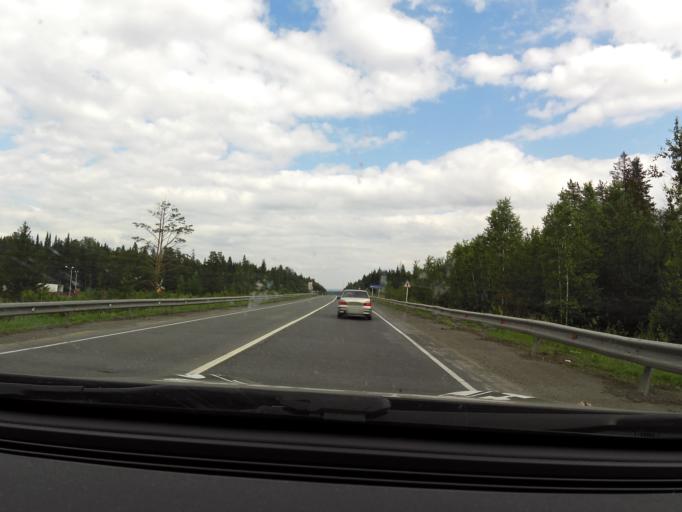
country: RU
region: Sverdlovsk
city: Atig
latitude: 56.7958
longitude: 59.4097
